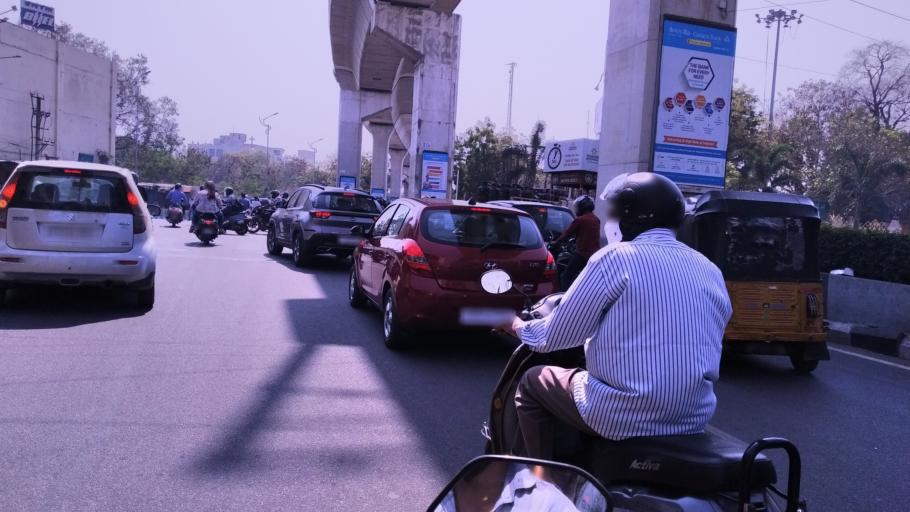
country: IN
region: Telangana
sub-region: Hyderabad
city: Malkajgiri
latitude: 17.4419
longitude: 78.4987
